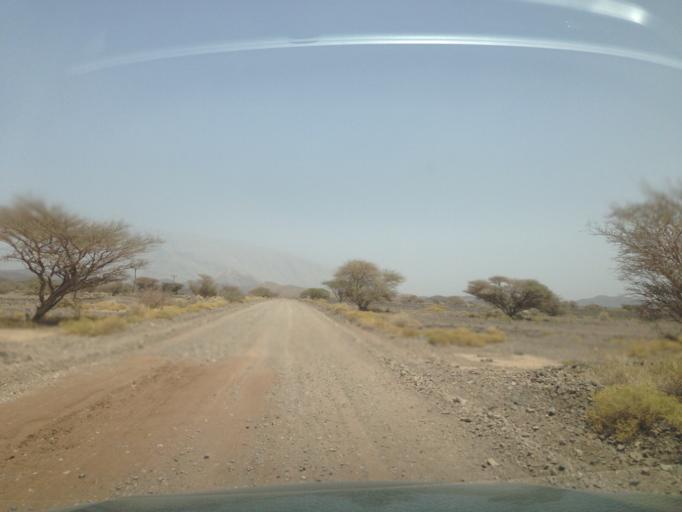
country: OM
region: Az Zahirah
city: `Ibri
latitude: 23.2174
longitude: 56.8300
